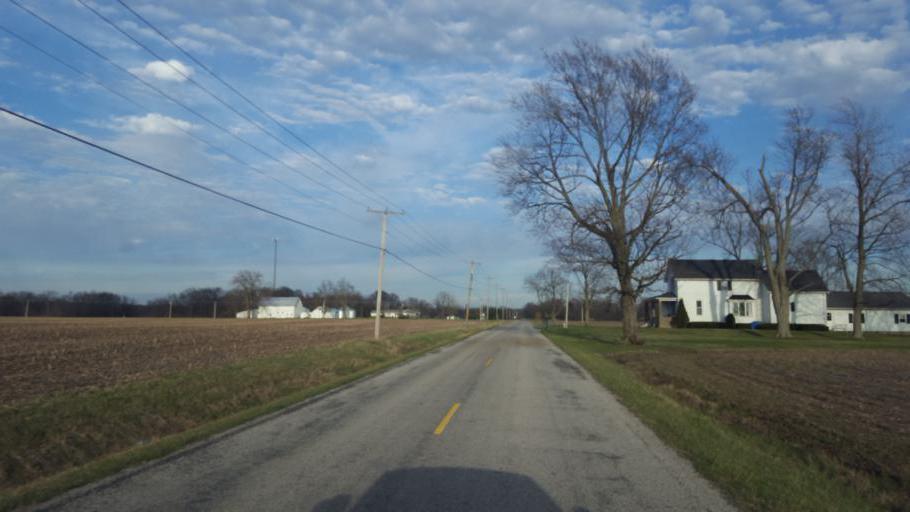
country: US
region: Ohio
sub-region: Marion County
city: Marion
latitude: 40.6162
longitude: -82.9948
